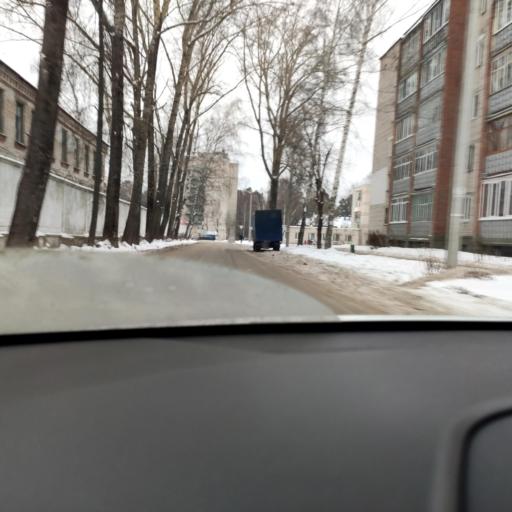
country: RU
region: Tatarstan
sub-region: Zelenodol'skiy Rayon
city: Zelenodolsk
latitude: 55.8550
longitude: 48.4935
